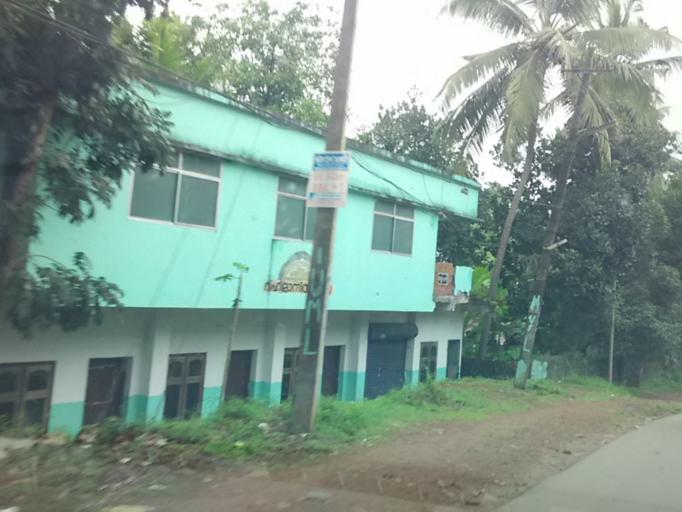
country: IN
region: Kerala
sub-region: Kozhikode
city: Kunnamangalam
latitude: 11.3070
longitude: 75.8964
